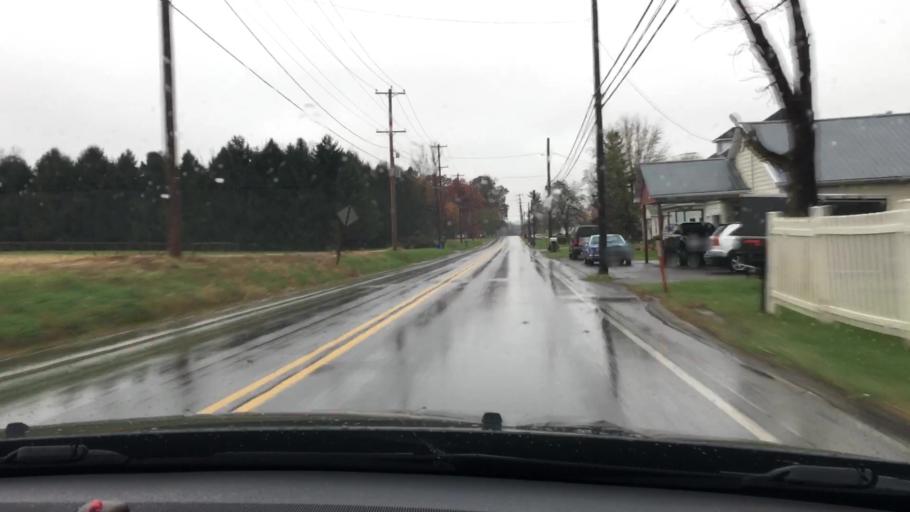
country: US
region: Pennsylvania
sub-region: York County
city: Susquehanna Trails
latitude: 39.8068
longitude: -76.3720
